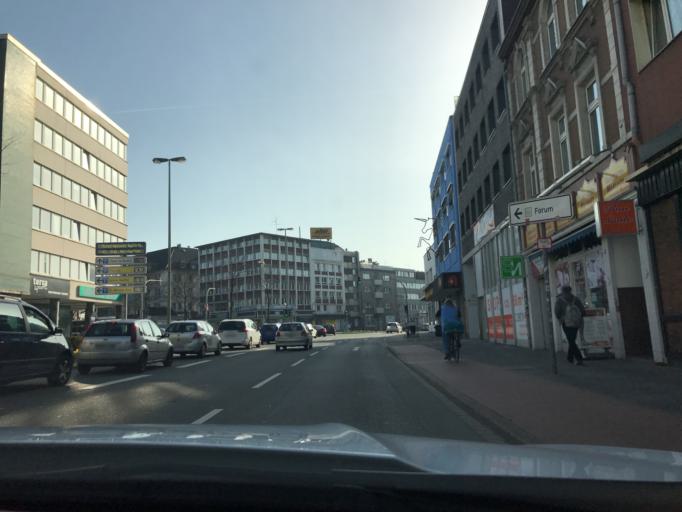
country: DE
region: North Rhine-Westphalia
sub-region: Regierungsbezirk Dusseldorf
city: Duisburg
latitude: 51.4331
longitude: 6.7614
